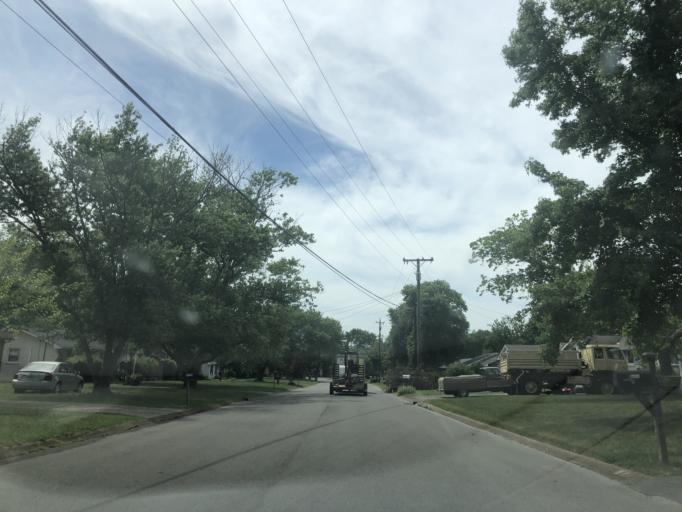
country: US
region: Tennessee
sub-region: Davidson County
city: Belle Meade
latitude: 36.0768
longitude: -86.9405
